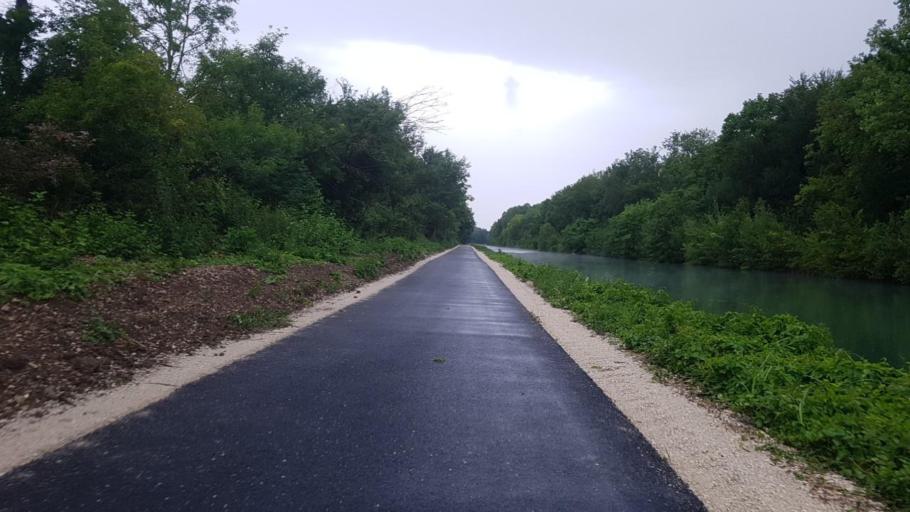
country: FR
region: Champagne-Ardenne
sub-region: Departement de la Marne
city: Sarry
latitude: 48.8657
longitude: 4.4678
